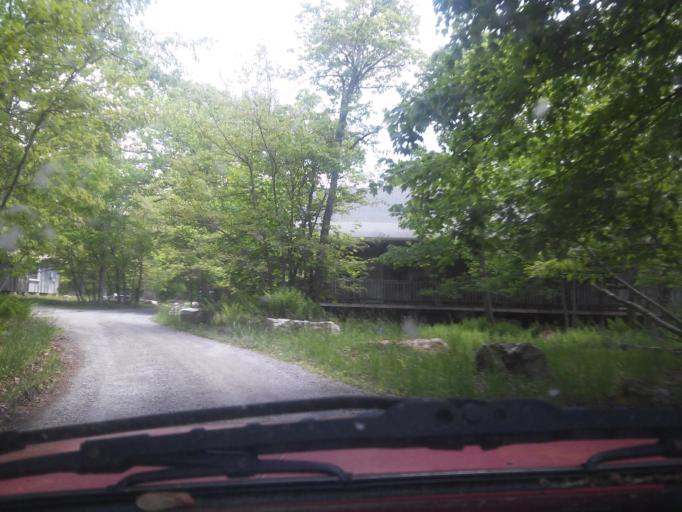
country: US
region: Virginia
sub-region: Giles County
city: Pembroke
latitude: 37.3750
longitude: -80.5226
